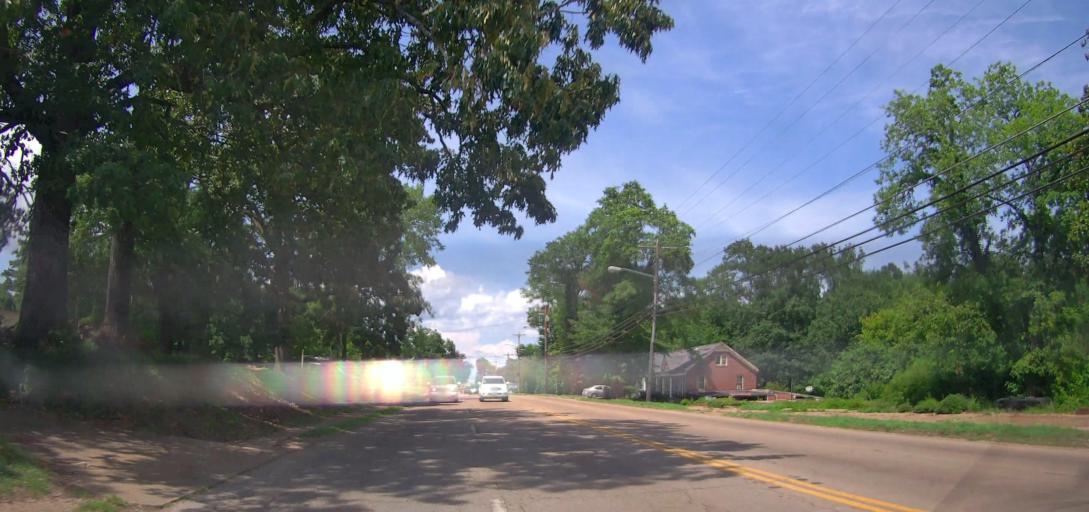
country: US
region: Mississippi
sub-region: Lee County
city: Verona
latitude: 34.1950
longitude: -88.7199
